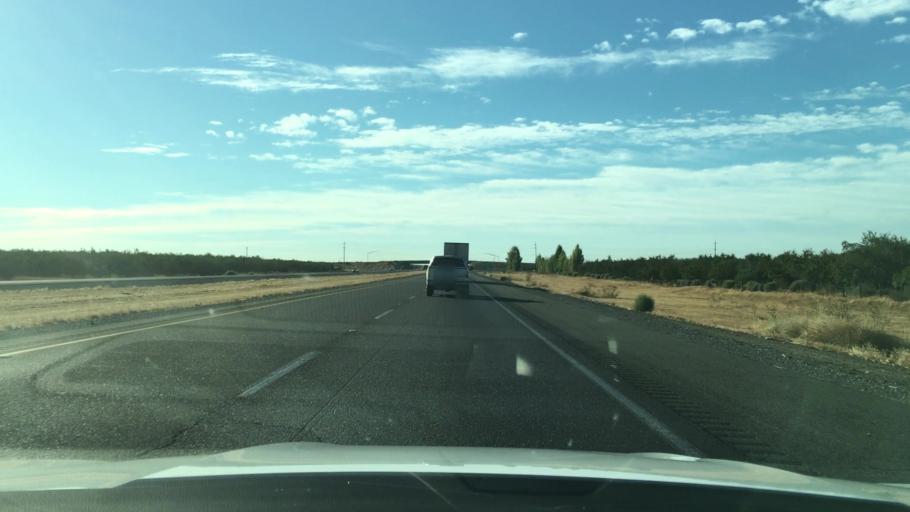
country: US
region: California
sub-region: Merced County
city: South Dos Palos
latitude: 36.7847
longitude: -120.7291
